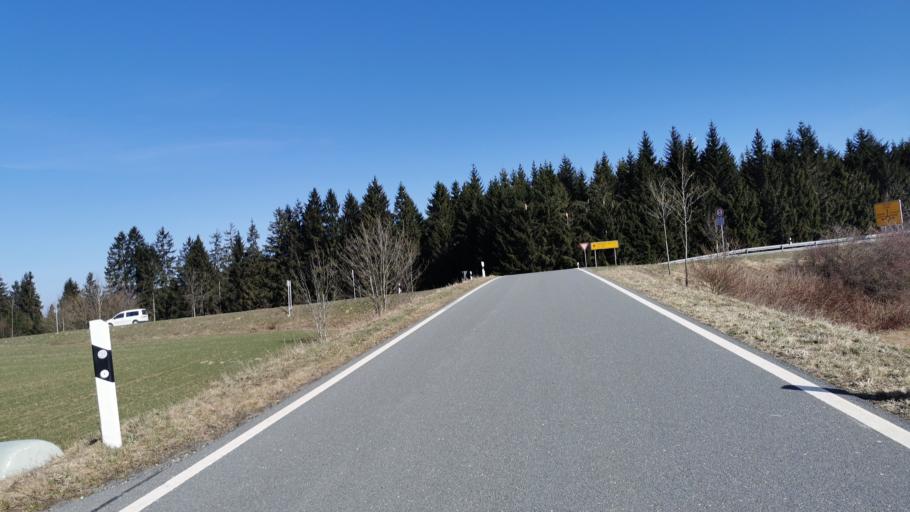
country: DE
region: Bavaria
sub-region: Upper Franconia
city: Reichenbach
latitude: 50.4472
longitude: 11.4046
